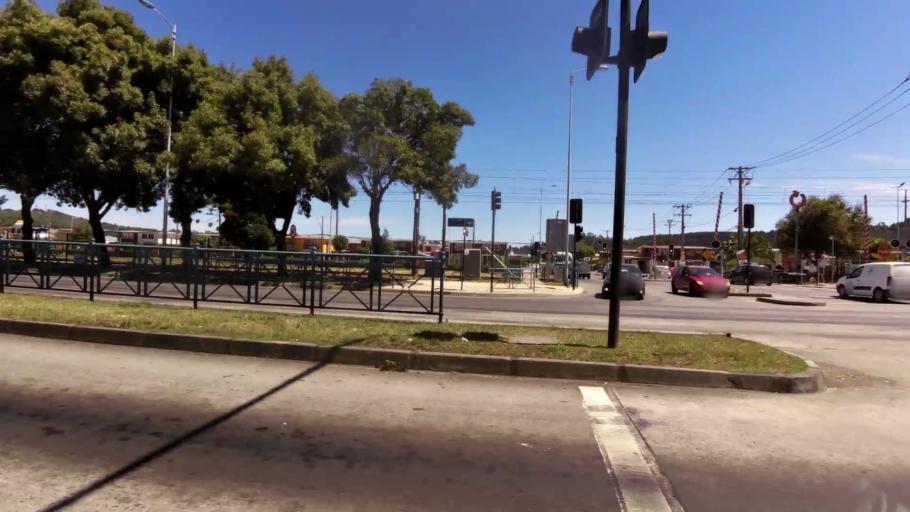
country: CL
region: Biobio
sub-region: Provincia de Concepcion
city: Talcahuano
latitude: -36.7572
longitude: -73.0910
